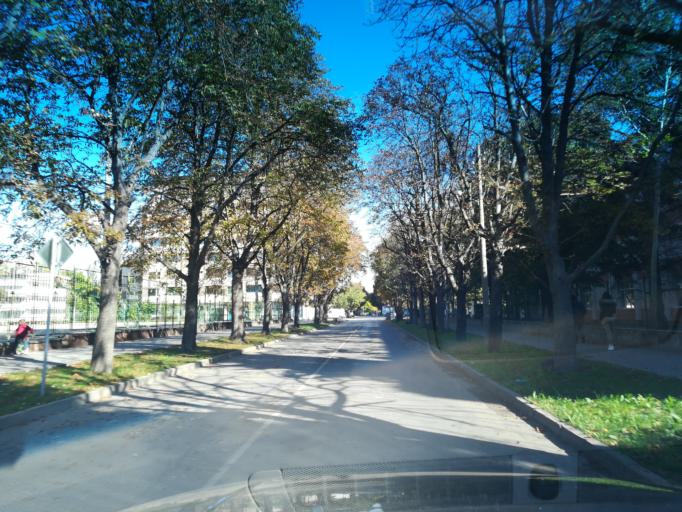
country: BG
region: Stara Zagora
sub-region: Obshtina Stara Zagora
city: Stara Zagora
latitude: 42.4305
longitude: 25.6402
